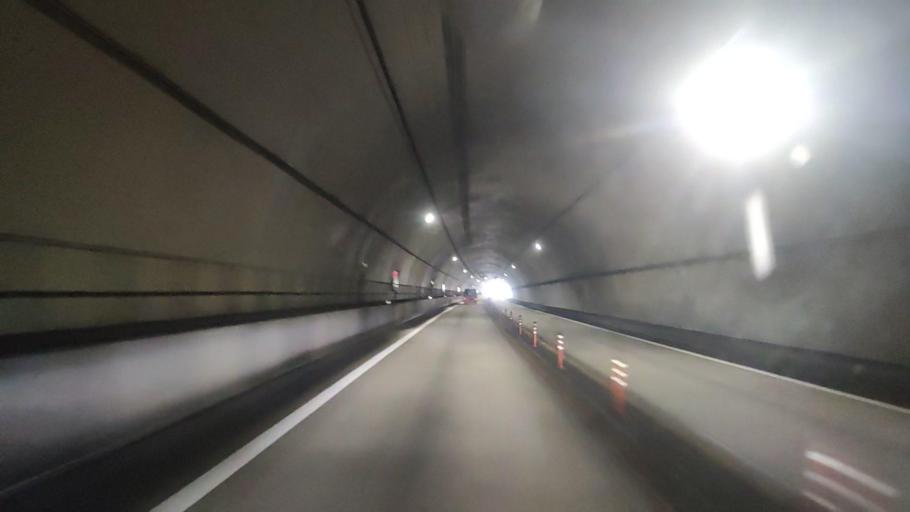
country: JP
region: Wakayama
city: Tanabe
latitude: 33.5511
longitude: 135.5142
